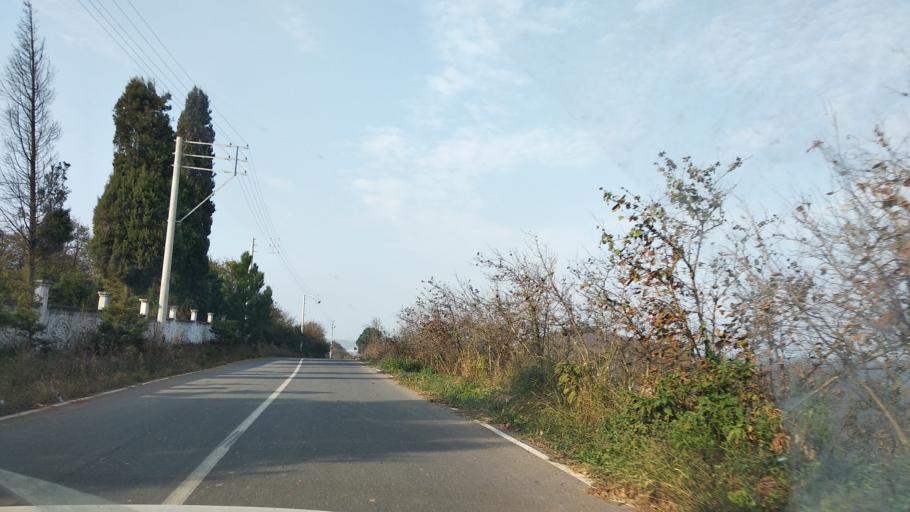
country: TR
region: Sakarya
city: Karasu
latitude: 41.0682
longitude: 30.6153
